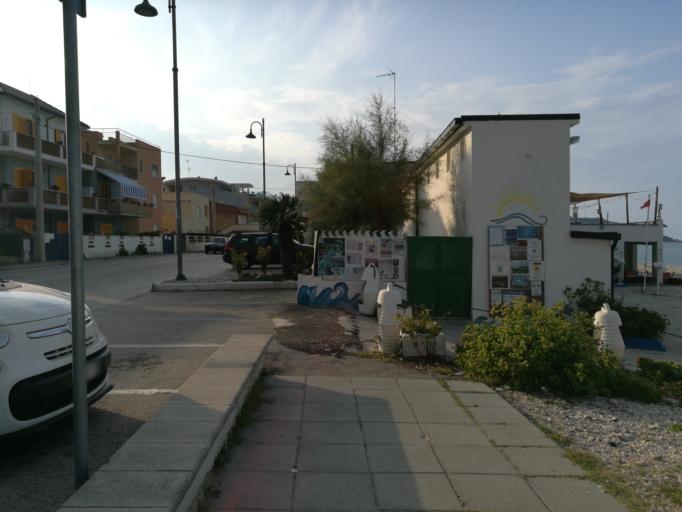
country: IT
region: Abruzzo
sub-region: Provincia di Chieti
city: Fossacesia
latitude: 42.2486
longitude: 14.5134
